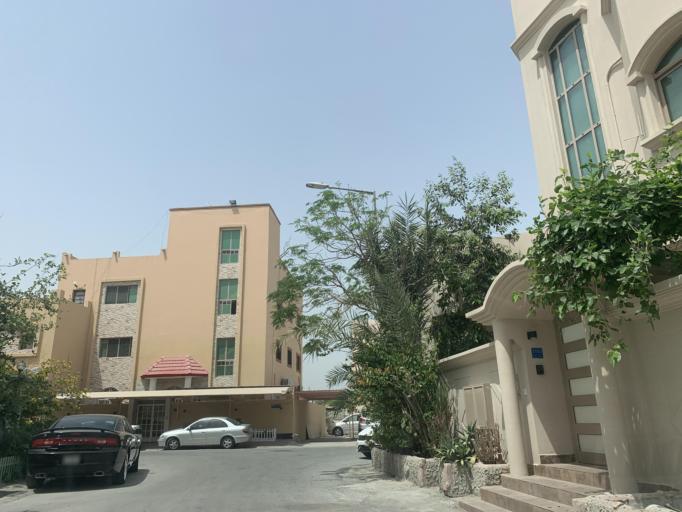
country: BH
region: Northern
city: Madinat `Isa
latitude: 26.1813
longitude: 50.5563
